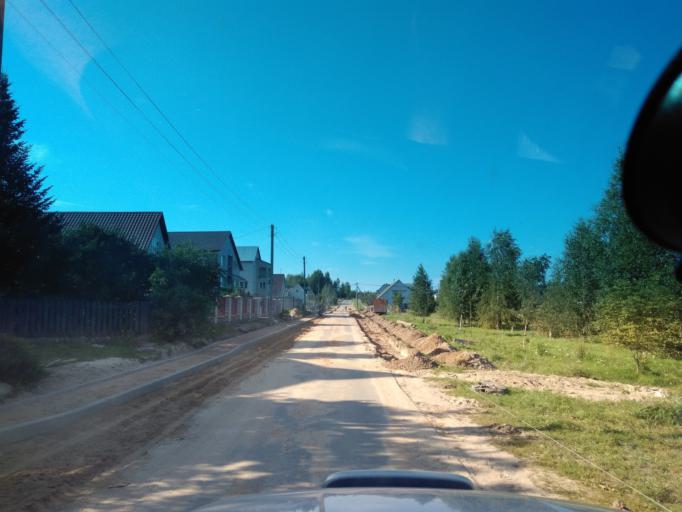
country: BY
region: Minsk
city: Uzda
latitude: 53.4656
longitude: 27.1944
